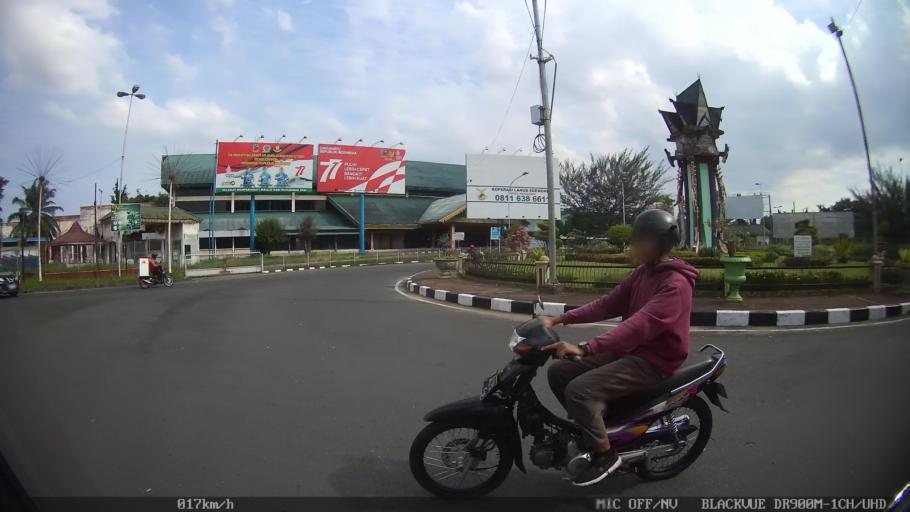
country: ID
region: North Sumatra
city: Medan
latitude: 3.5695
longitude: 98.6783
